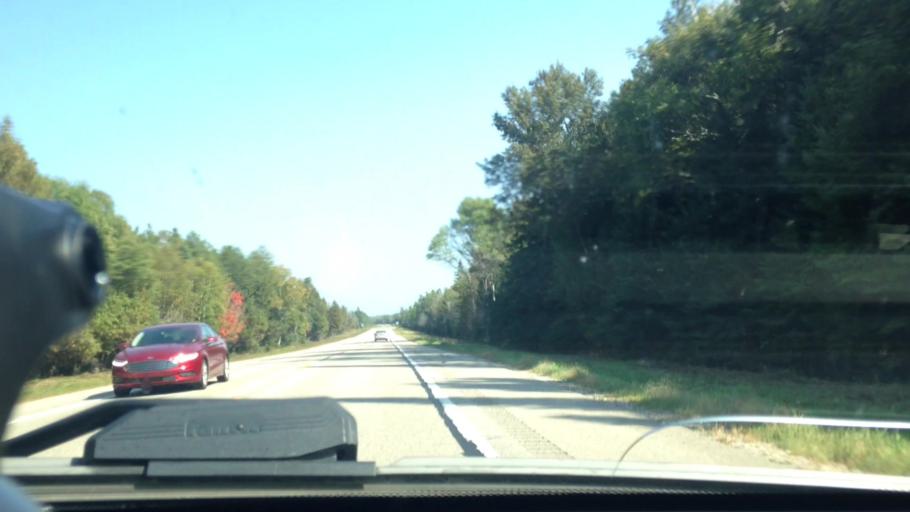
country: US
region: Michigan
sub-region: Luce County
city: Newberry
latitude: 46.3035
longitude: -85.2479
